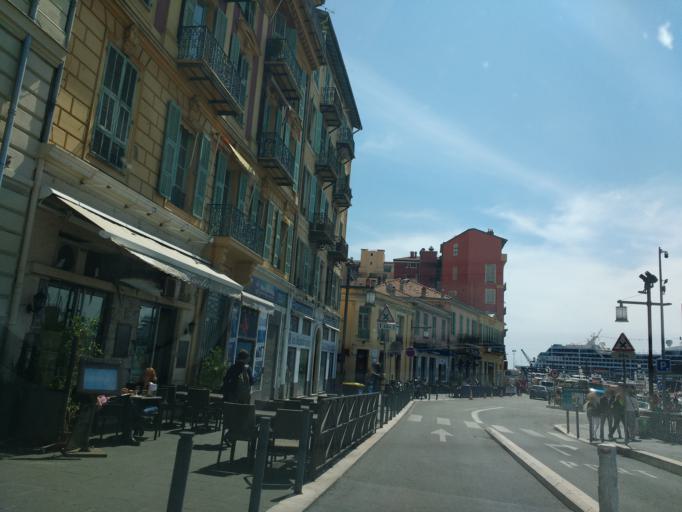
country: FR
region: Provence-Alpes-Cote d'Azur
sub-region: Departement des Alpes-Maritimes
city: Nice
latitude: 43.6970
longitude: 7.2863
